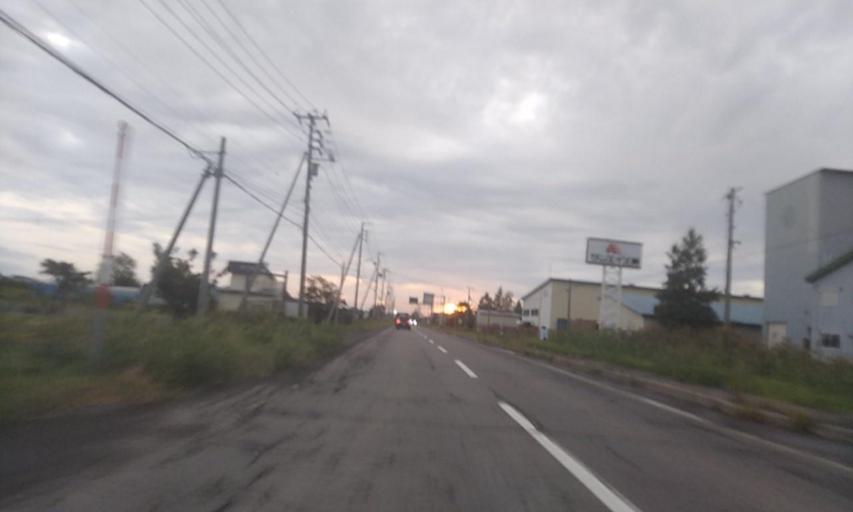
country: JP
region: Hokkaido
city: Abashiri
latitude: 43.9015
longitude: 144.6788
